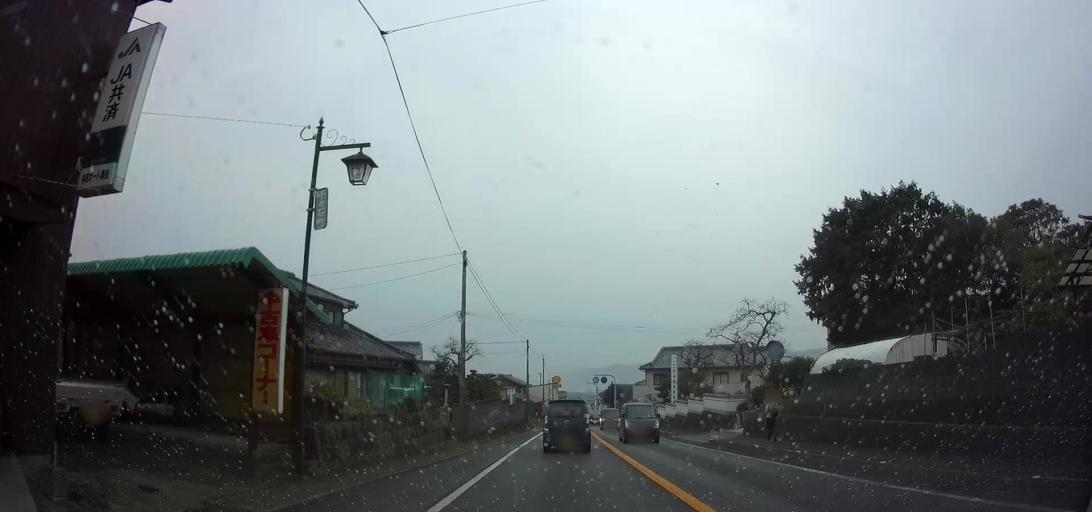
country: JP
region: Nagasaki
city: Shimabara
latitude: 32.7846
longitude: 130.2025
